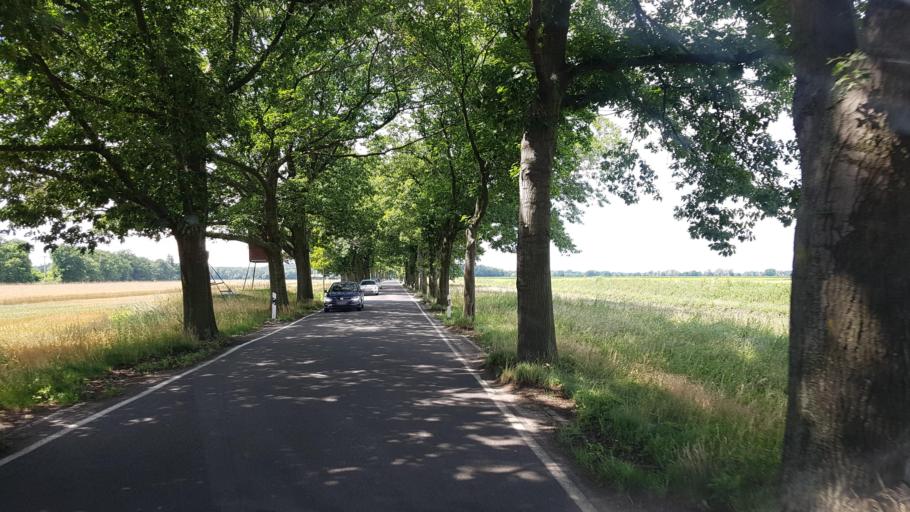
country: DE
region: Brandenburg
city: Senftenberg
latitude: 51.4869
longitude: 14.0969
